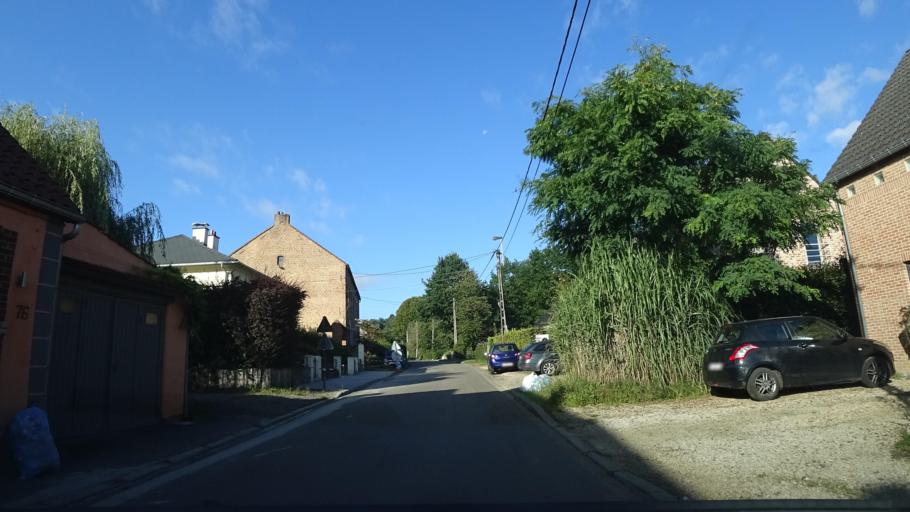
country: BE
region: Wallonia
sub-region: Province du Brabant Wallon
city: Court-Saint-Etienne
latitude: 50.6376
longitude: 4.5254
